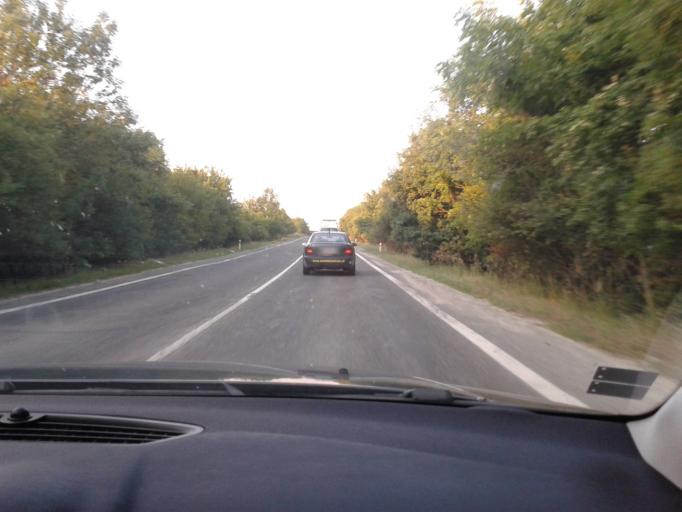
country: SK
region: Nitriansky
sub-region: Okres Nitra
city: Nitra
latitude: 48.3599
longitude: 18.1832
